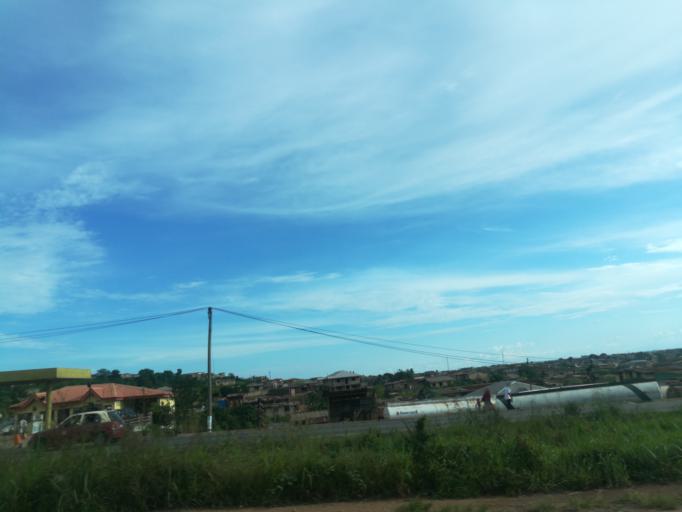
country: NG
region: Oyo
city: Ibadan
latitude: 7.3438
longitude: 3.9130
